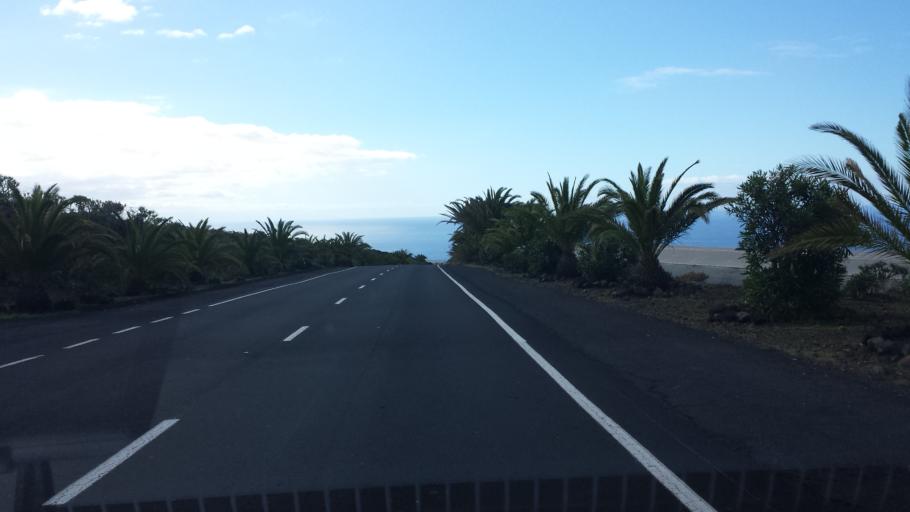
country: ES
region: Canary Islands
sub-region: Provincia de Santa Cruz de Tenerife
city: Tazacorte
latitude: 28.6047
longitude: -17.9076
